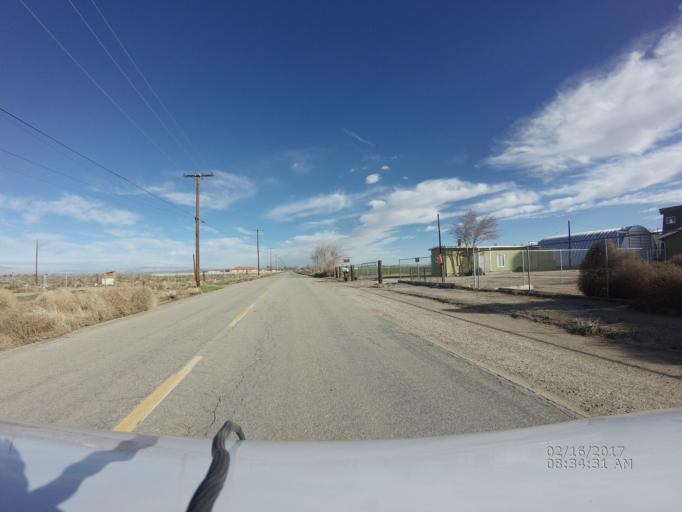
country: US
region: California
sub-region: Los Angeles County
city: Lancaster
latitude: 34.7270
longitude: -118.0054
